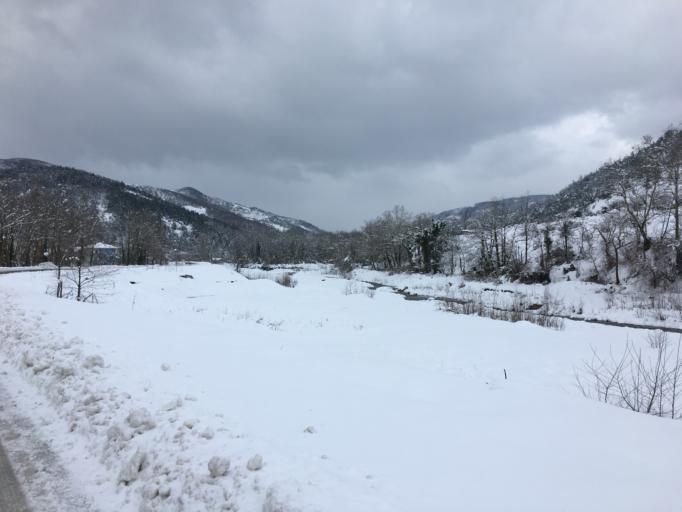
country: TR
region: Samsun
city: Alacam
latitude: 41.5979
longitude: 35.5936
